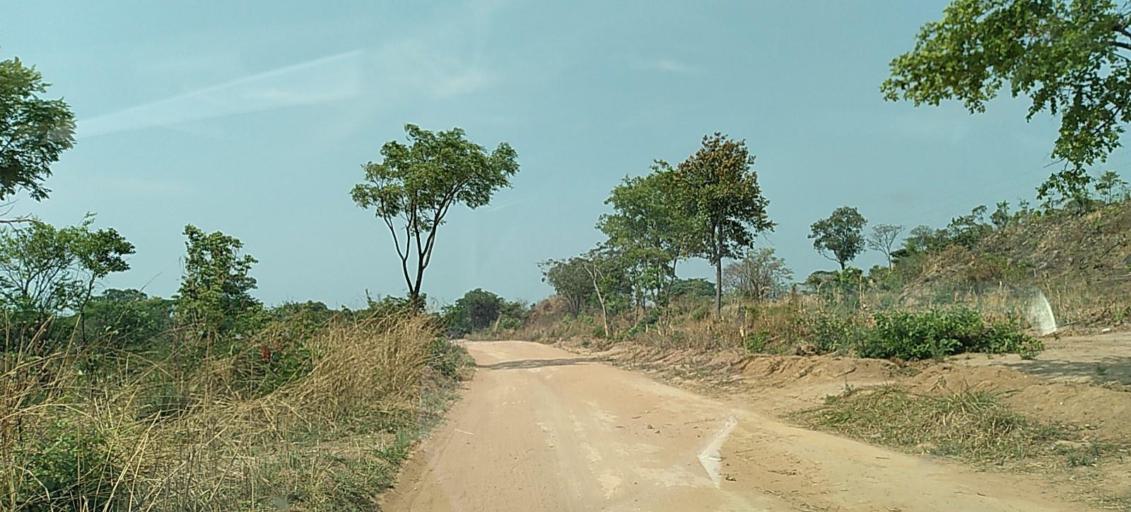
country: ZM
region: Copperbelt
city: Chililabombwe
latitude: -12.3327
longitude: 27.7297
